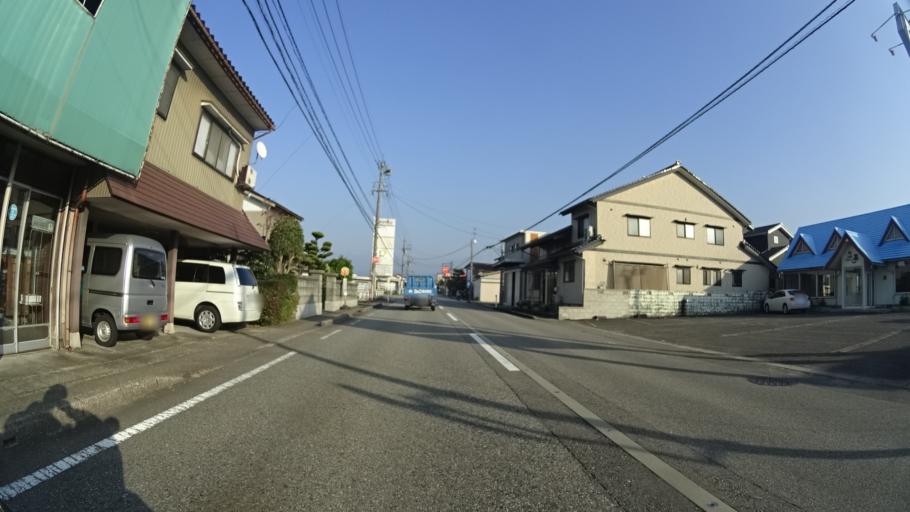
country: JP
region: Toyama
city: Kamiichi
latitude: 36.6642
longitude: 137.3060
